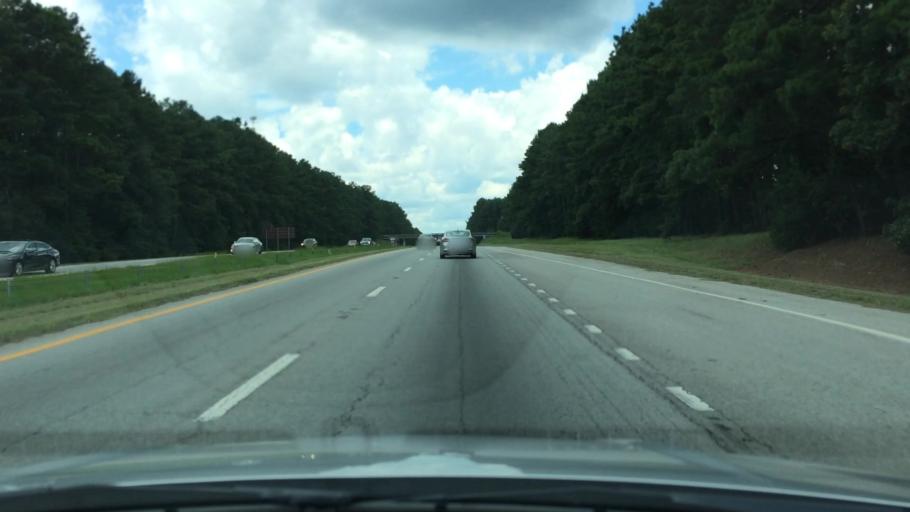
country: US
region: South Carolina
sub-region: Newberry County
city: Newberry
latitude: 34.3143
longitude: -81.5798
